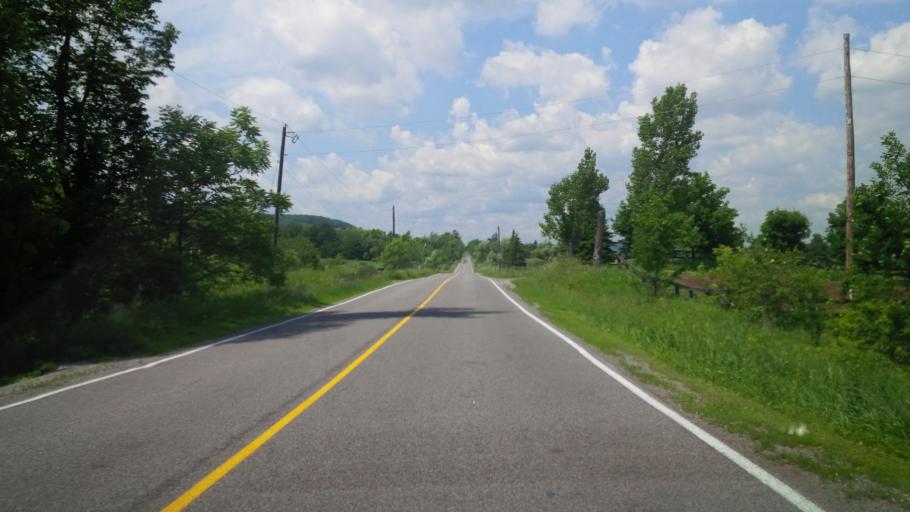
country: CA
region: Ontario
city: Burlington
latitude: 43.4113
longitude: -79.8495
